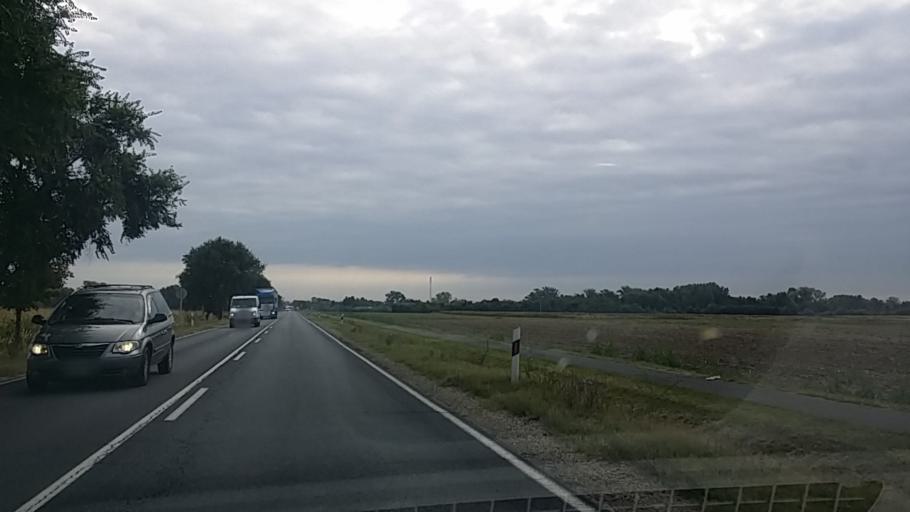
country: HU
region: Gyor-Moson-Sopron
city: Kapuvar
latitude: 47.5892
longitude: 16.9993
